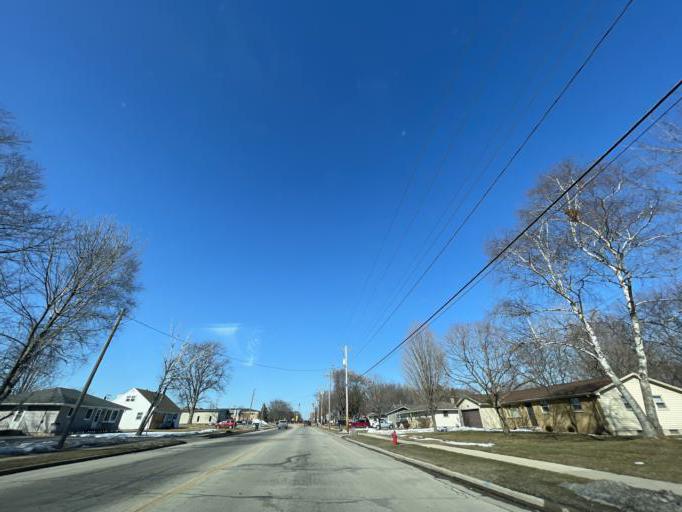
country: US
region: Wisconsin
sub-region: Brown County
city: Howard
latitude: 44.5714
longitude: -88.0847
